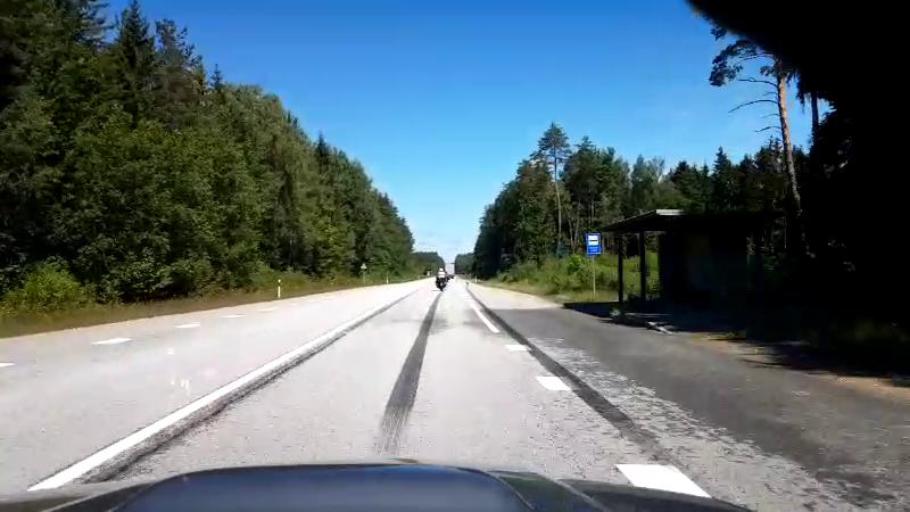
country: LV
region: Saulkrastu
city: Saulkrasti
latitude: 57.4225
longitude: 24.4289
